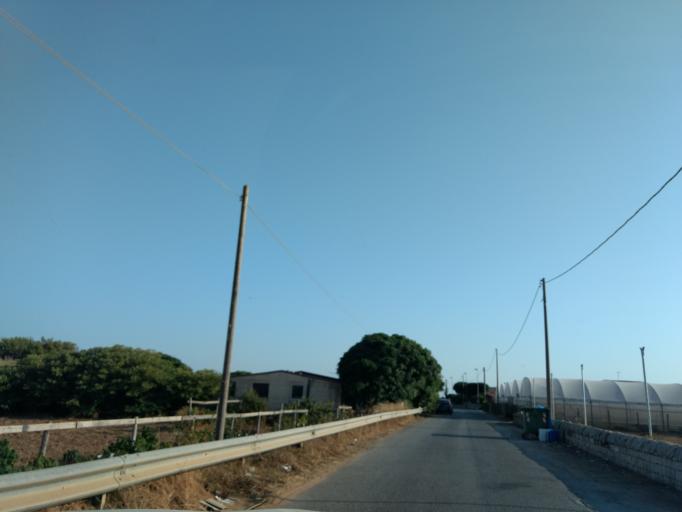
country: IT
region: Sicily
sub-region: Ragusa
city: Donnalucata
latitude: 36.7494
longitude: 14.6638
